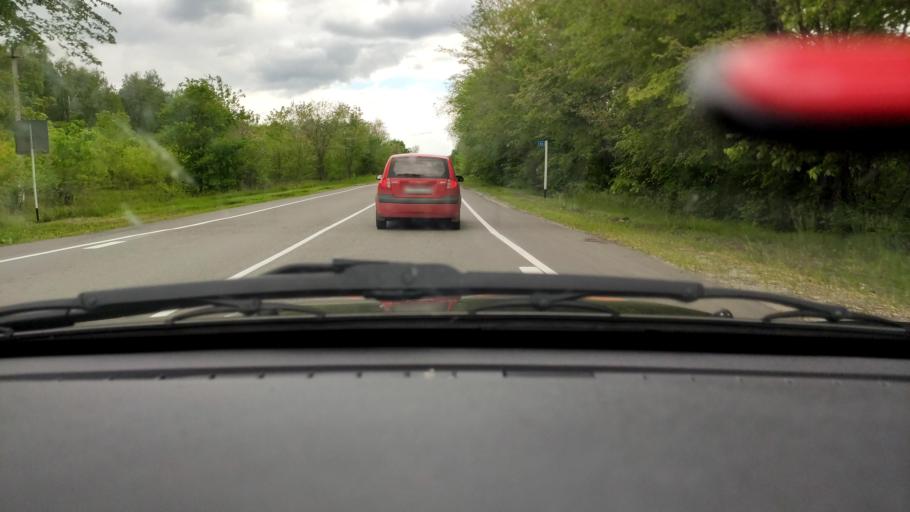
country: RU
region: Belgorod
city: Krasnoye
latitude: 51.0678
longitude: 38.8076
